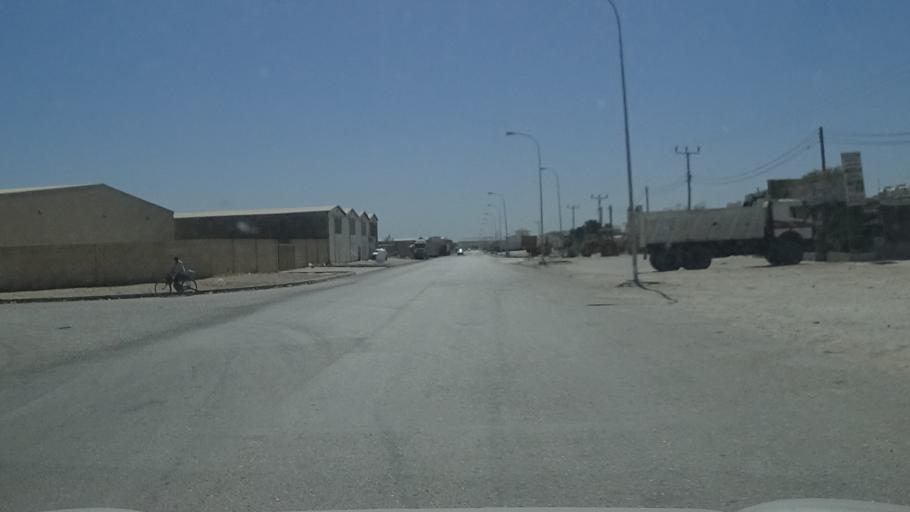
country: OM
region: Zufar
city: Salalah
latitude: 17.0321
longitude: 54.0388
